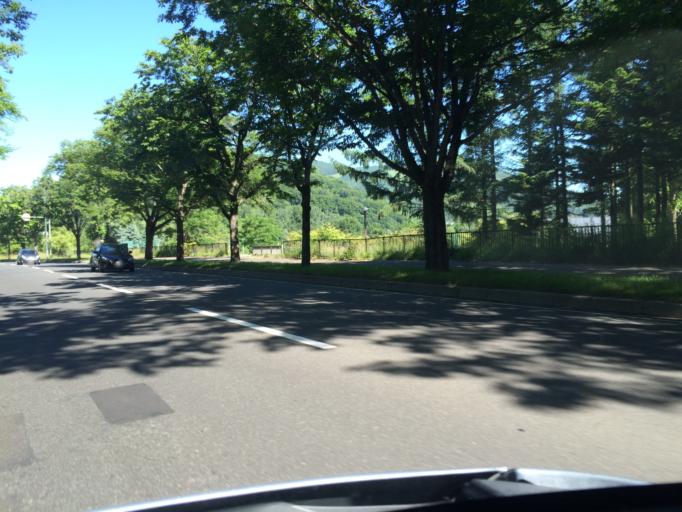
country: JP
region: Hokkaido
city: Sapporo
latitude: 42.9984
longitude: 141.3459
